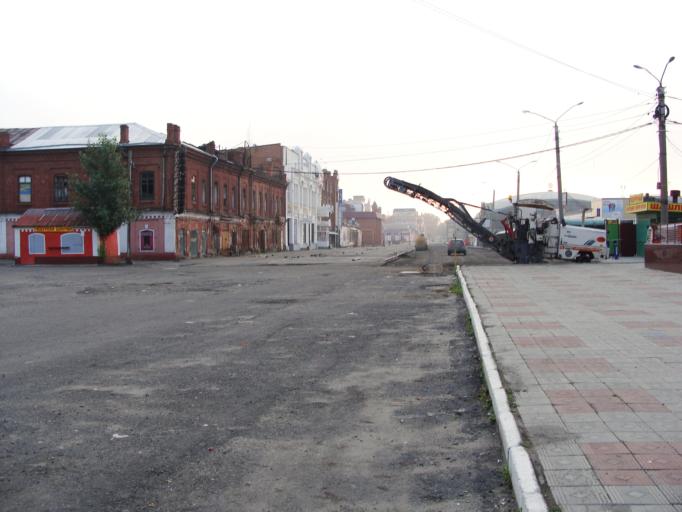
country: RU
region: Altai Krai
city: Zaton
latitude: 53.3287
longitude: 83.7918
